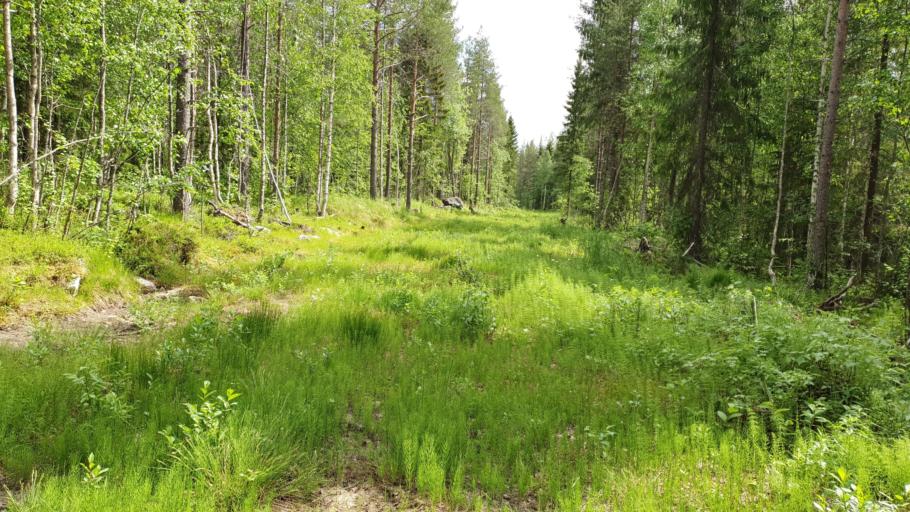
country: FI
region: Kainuu
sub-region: Kehys-Kainuu
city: Kuhmo
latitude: 64.4426
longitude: 29.6882
